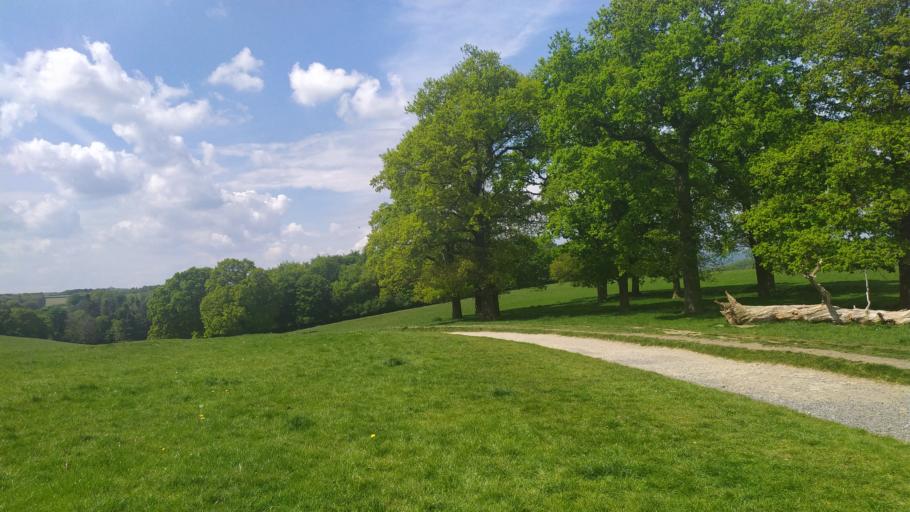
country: GB
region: England
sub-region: City and Borough of Leeds
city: Shadwell
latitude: 53.8843
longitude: -1.5152
